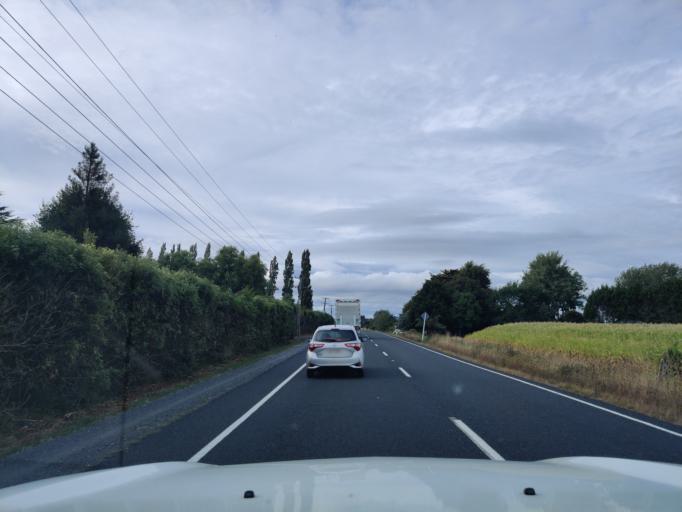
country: NZ
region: Waikato
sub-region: Hamilton City
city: Hamilton
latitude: -37.7080
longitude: 175.3380
